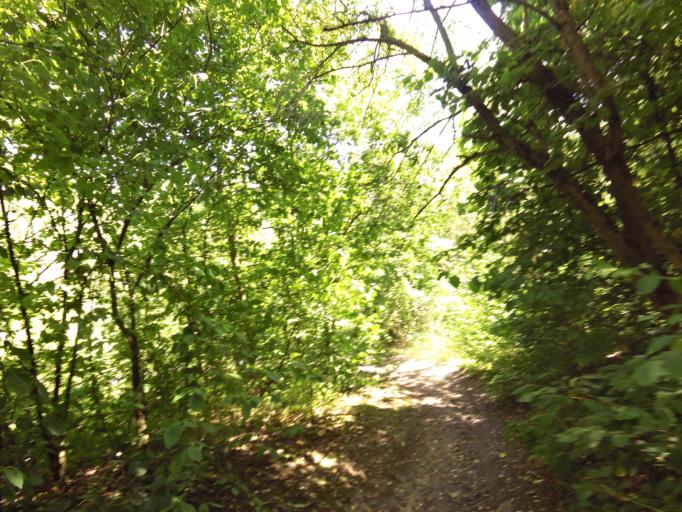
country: NL
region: Limburg
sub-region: Gemeente Kerkrade
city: Kerkrade
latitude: 50.8762
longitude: 6.0279
